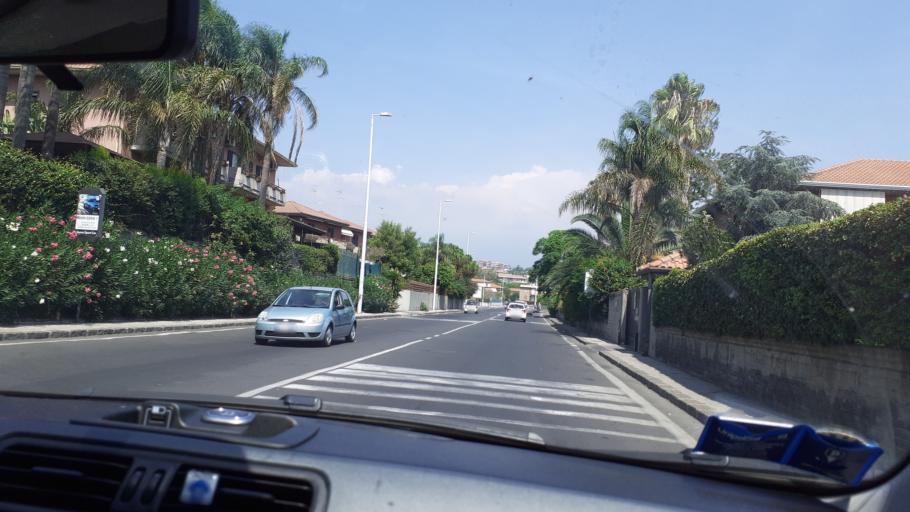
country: IT
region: Sicily
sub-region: Catania
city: Catania
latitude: 37.5139
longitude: 15.0562
